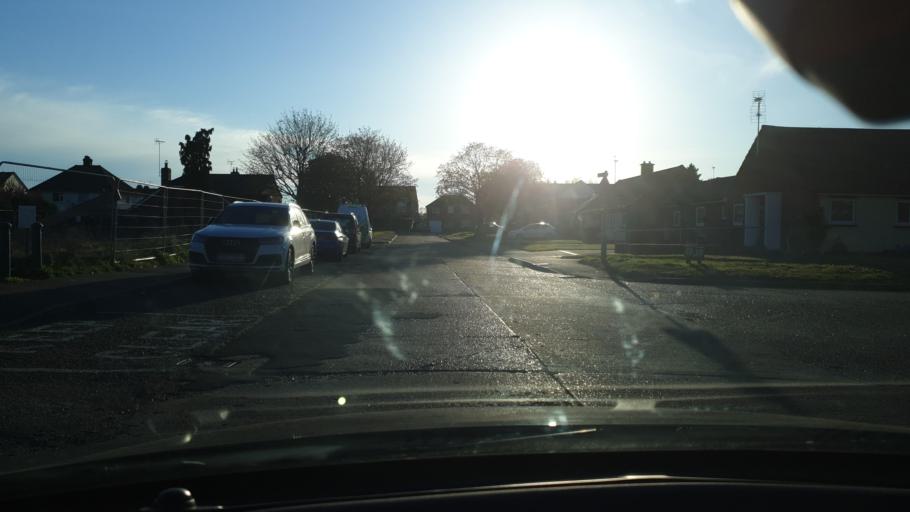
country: GB
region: England
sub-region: Essex
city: Manningtree
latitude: 51.9393
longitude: 1.0525
